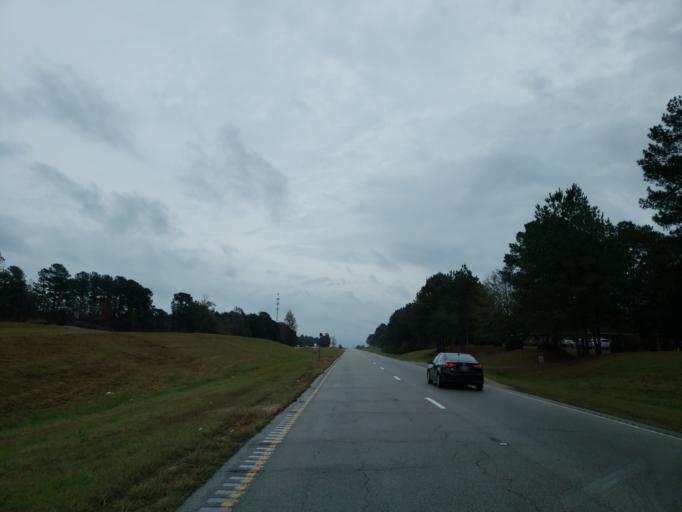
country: US
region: Mississippi
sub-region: Jones County
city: Sharon
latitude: 31.7053
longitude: -88.9303
